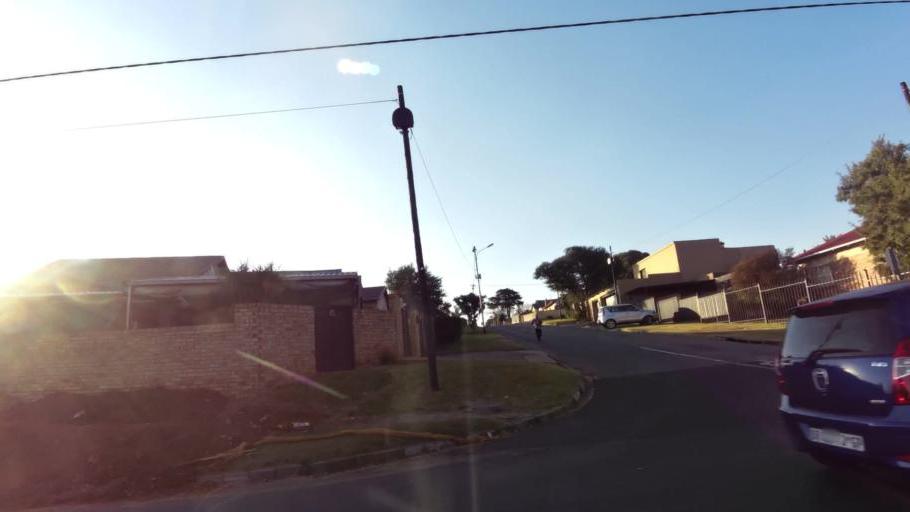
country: ZA
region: Gauteng
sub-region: City of Johannesburg Metropolitan Municipality
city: Roodepoort
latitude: -26.1733
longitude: 27.9465
